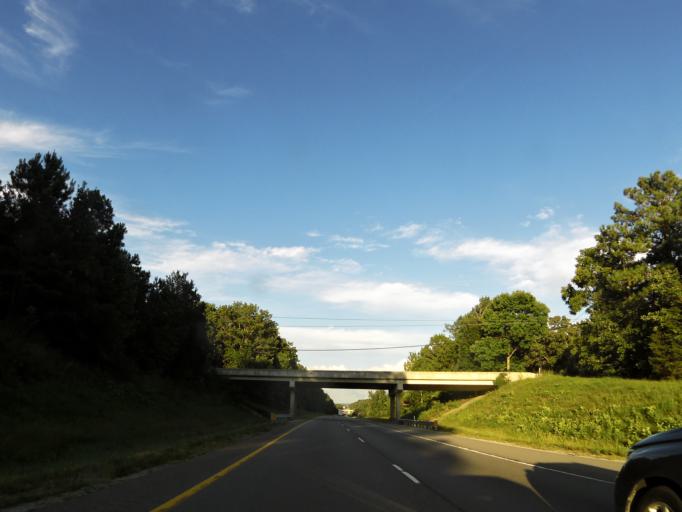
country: US
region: Tennessee
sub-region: Putnam County
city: Cookeville
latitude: 36.1358
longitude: -85.5462
